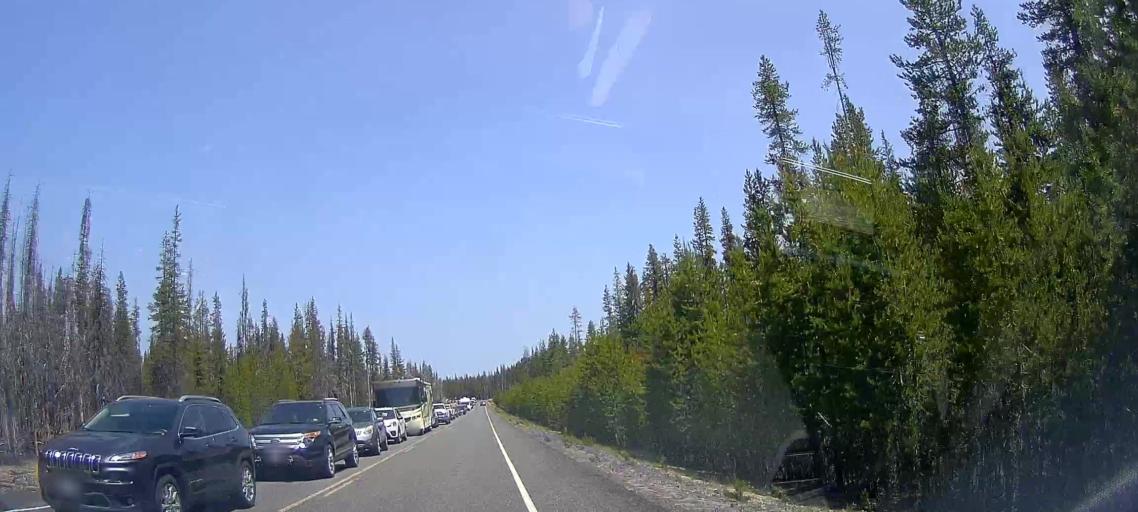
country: US
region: Oregon
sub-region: Lane County
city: Oakridge
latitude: 43.0832
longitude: -122.1169
